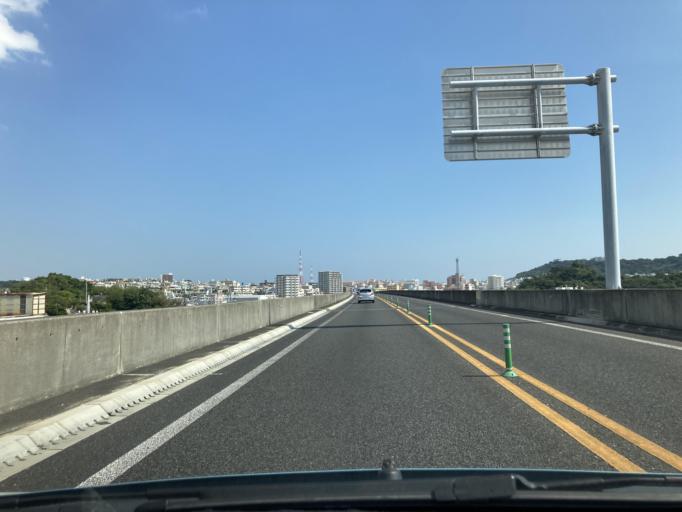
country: JP
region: Okinawa
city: Tomigusuku
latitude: 26.1751
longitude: 127.6664
